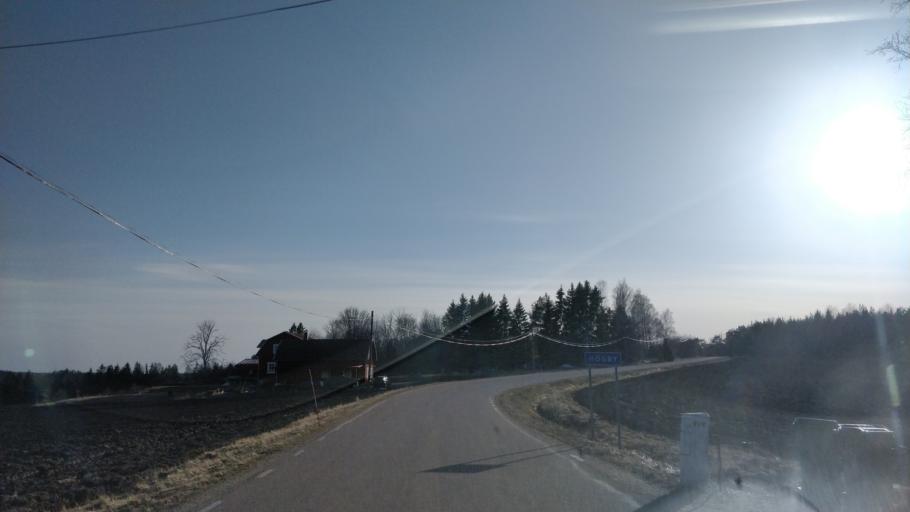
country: SE
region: Uppsala
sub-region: Enkopings Kommun
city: Orsundsbro
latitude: 59.7504
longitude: 17.2344
